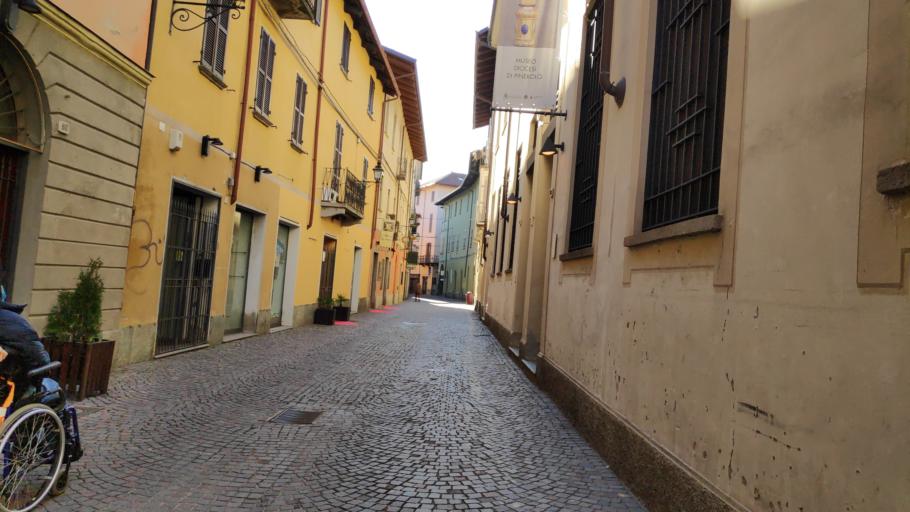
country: IT
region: Piedmont
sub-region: Provincia di Torino
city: Pinerolo
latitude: 44.8873
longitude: 7.3309
